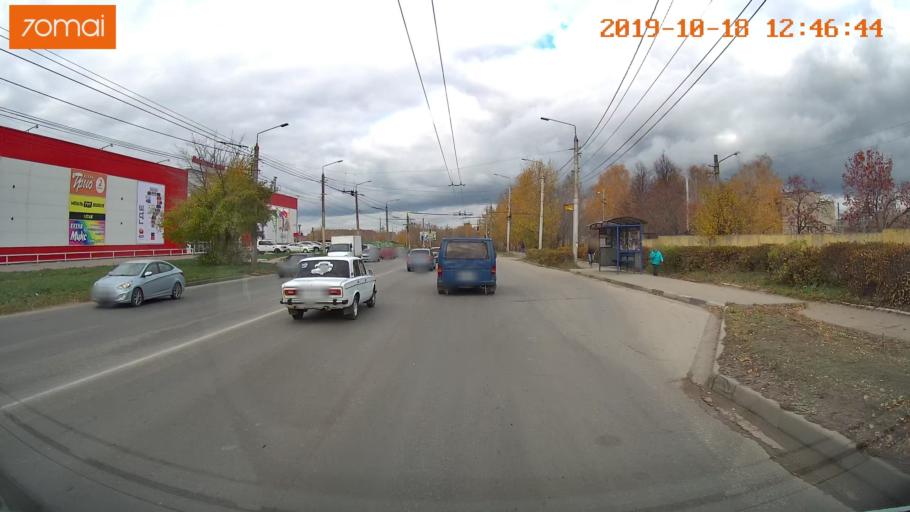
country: RU
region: Rjazan
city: Ryazan'
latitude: 54.6556
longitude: 39.6643
